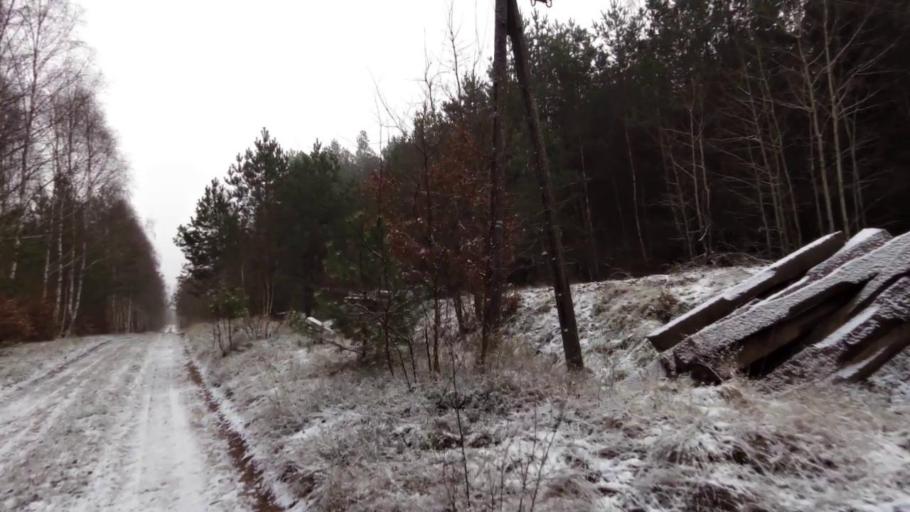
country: PL
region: West Pomeranian Voivodeship
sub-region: Powiat drawski
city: Wierzchowo
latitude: 53.4423
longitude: 16.1960
